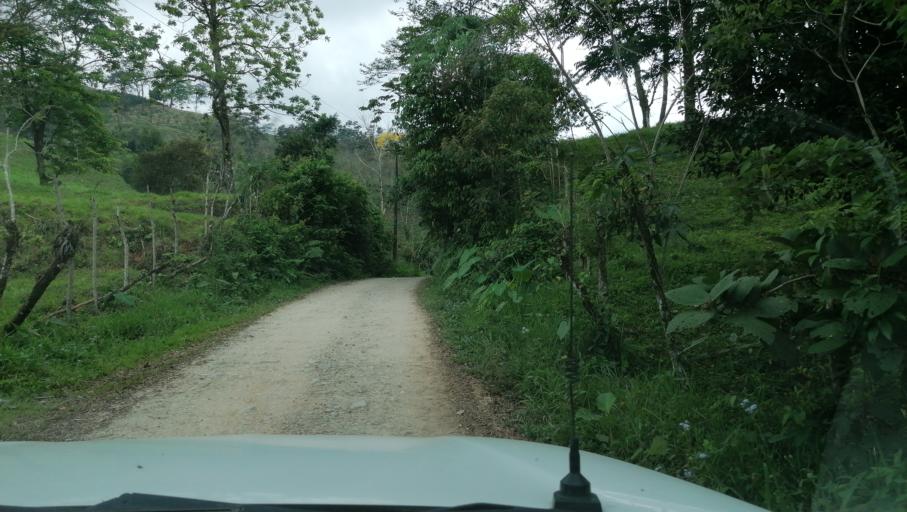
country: MX
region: Chiapas
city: Ocotepec
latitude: 17.2794
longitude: -93.2290
